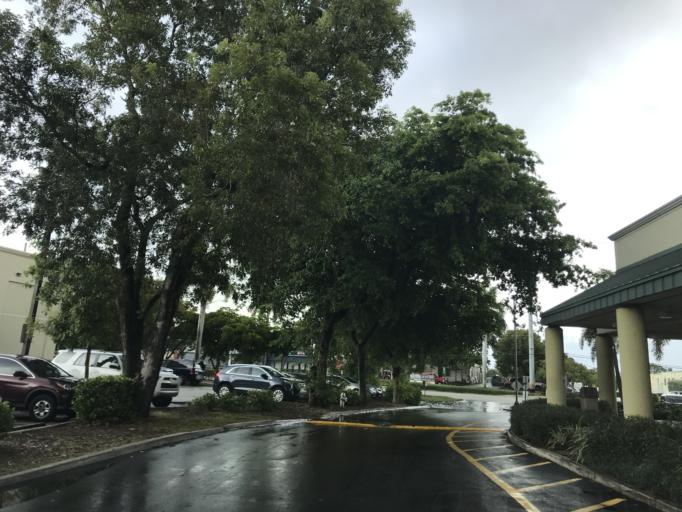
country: US
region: Florida
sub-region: Palm Beach County
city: Delray Beach
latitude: 26.4591
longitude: -80.0944
